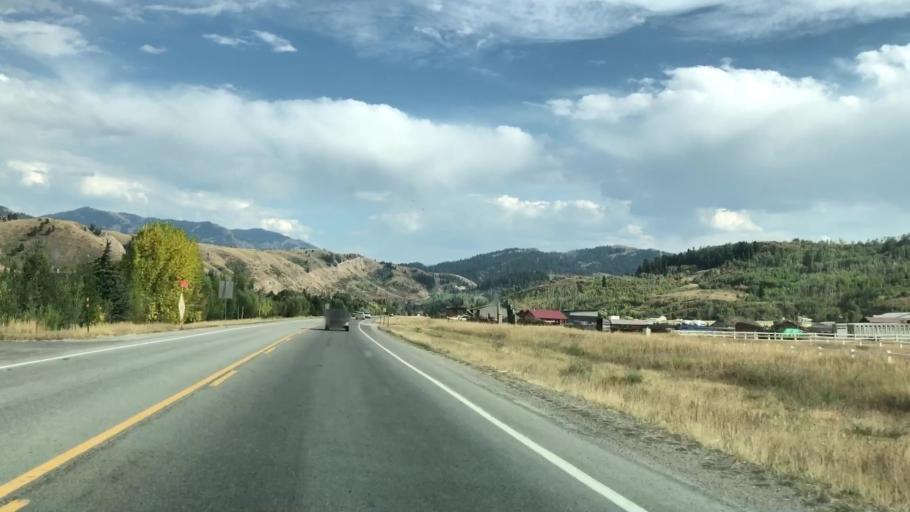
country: US
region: Wyoming
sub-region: Teton County
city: South Park
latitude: 43.3694
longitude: -110.7375
